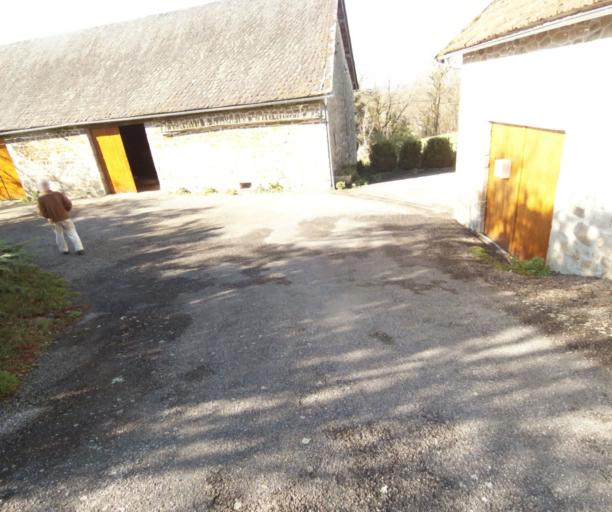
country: FR
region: Limousin
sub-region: Departement de la Correze
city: Correze
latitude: 45.2697
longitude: 1.8844
